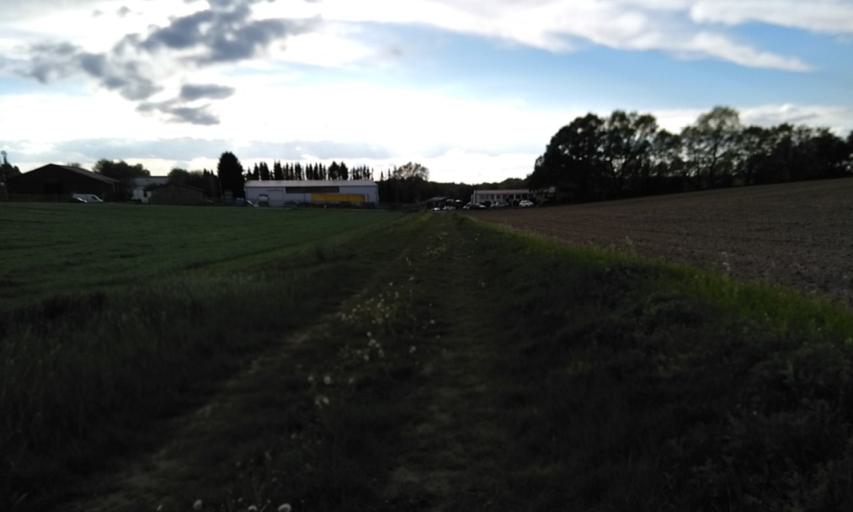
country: DE
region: Lower Saxony
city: Harsefeld
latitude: 53.4617
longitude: 9.5269
